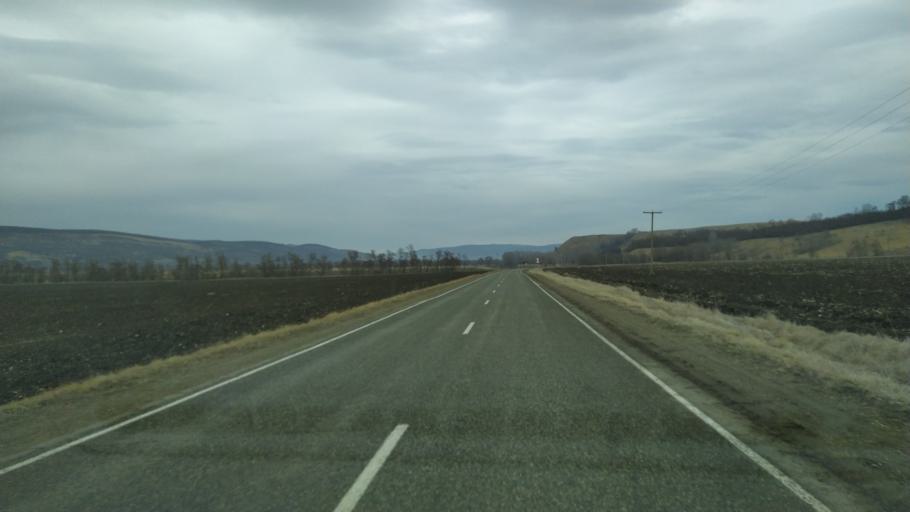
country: RU
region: Krasnodarskiy
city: Peredovaya
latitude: 44.0991
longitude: 41.4033
